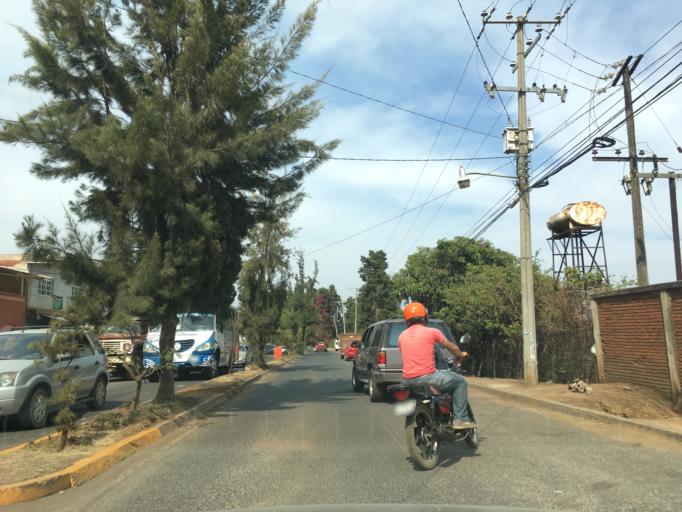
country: MX
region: Michoacan
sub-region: Uruapan
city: Uruapan
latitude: 19.3847
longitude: -102.0734
